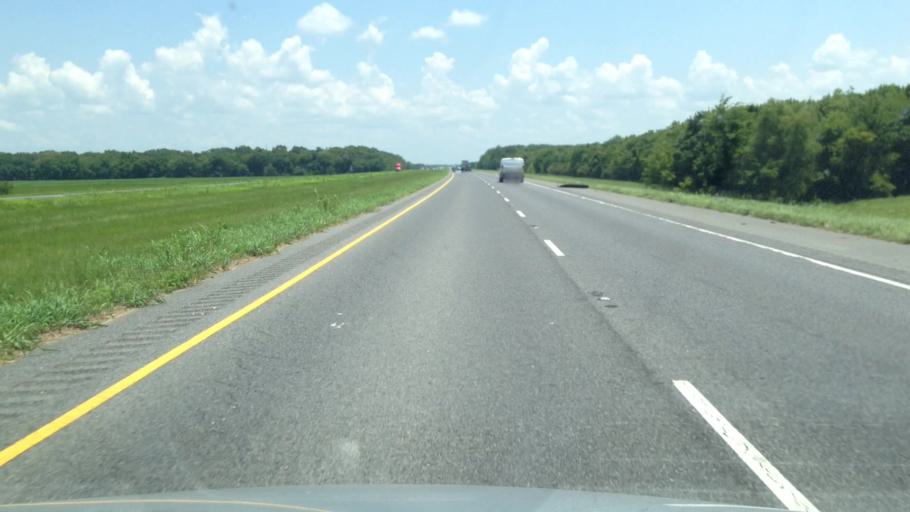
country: US
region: Louisiana
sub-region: Evangeline Parish
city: Ville Platte
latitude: 30.8013
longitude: -92.2103
